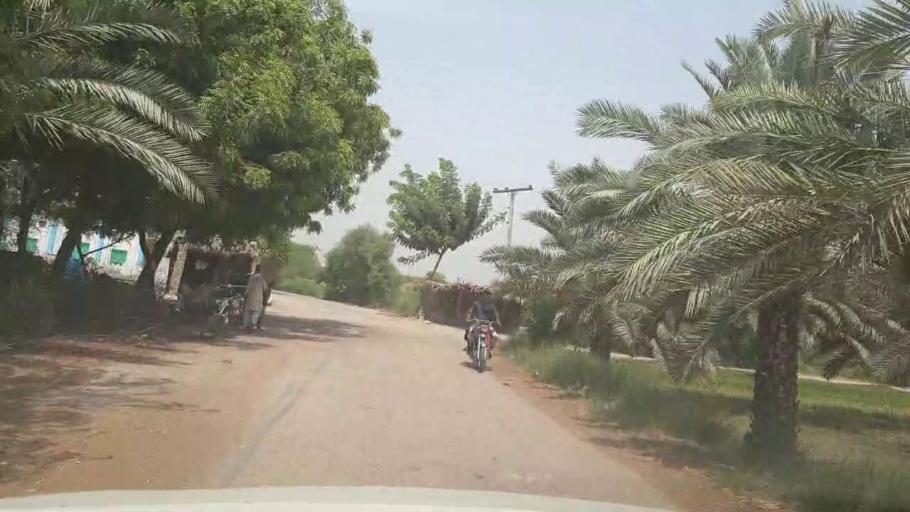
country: PK
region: Sindh
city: Kot Diji
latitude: 27.3657
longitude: 68.6498
